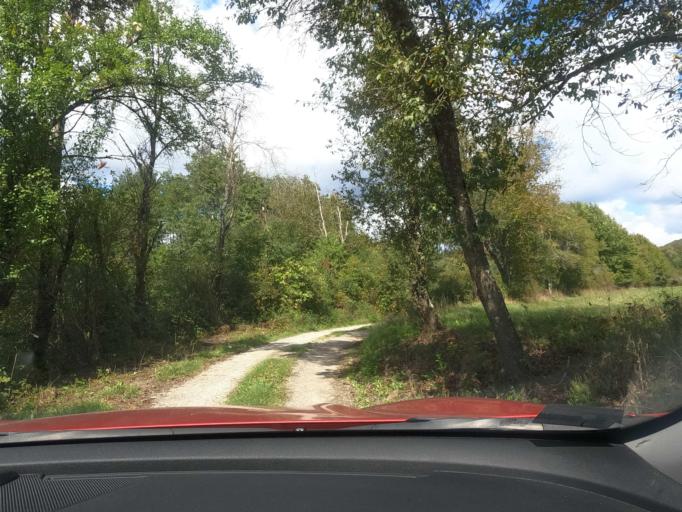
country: BA
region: Federation of Bosnia and Herzegovina
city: Velika Kladusa
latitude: 45.2319
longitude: 15.7738
